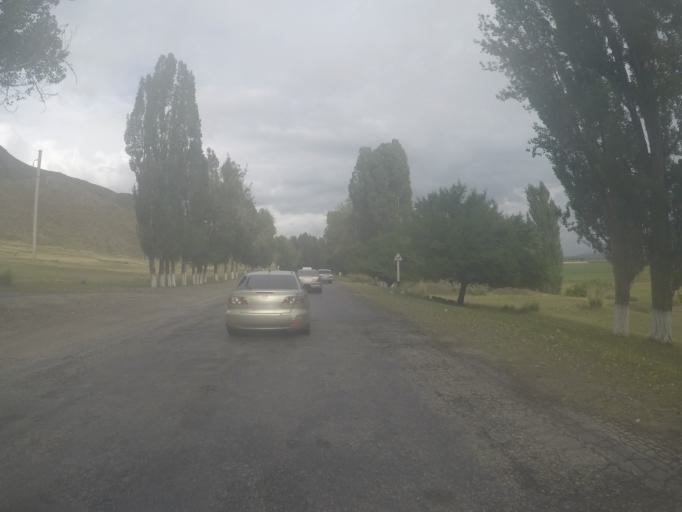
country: KG
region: Ysyk-Koel
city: Tyup
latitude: 42.7438
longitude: 78.0473
